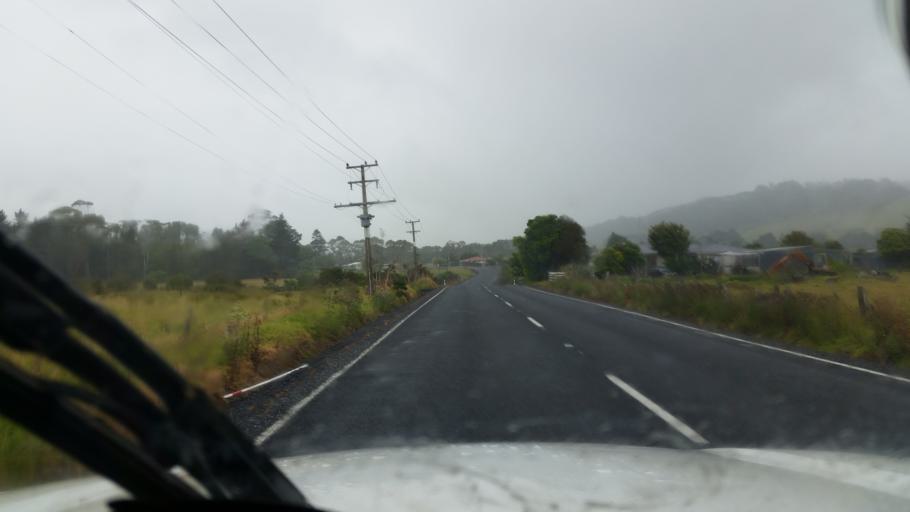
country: NZ
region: Northland
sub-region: Far North District
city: Ahipara
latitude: -35.1767
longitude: 173.1743
